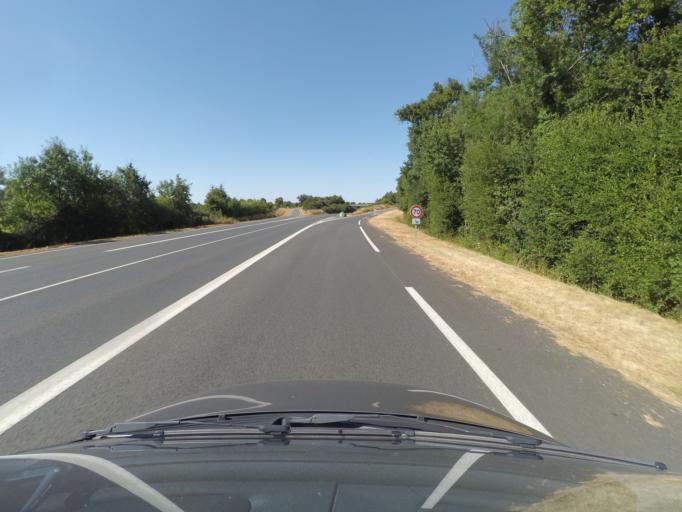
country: FR
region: Pays de la Loire
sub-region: Departement de la Vendee
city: Bouffere
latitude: 46.9820
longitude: -1.3546
